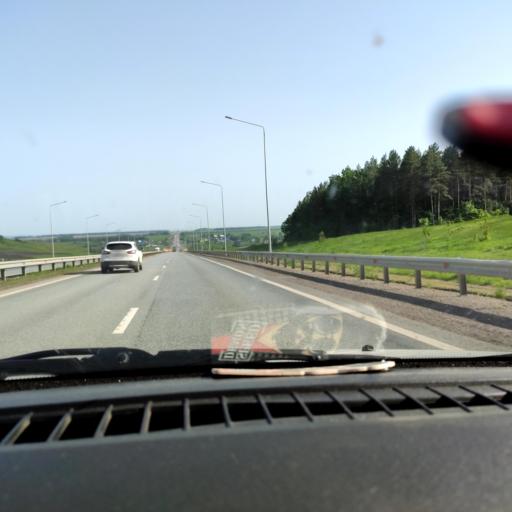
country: RU
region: Bashkortostan
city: Tolbazy
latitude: 53.8299
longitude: 55.9242
